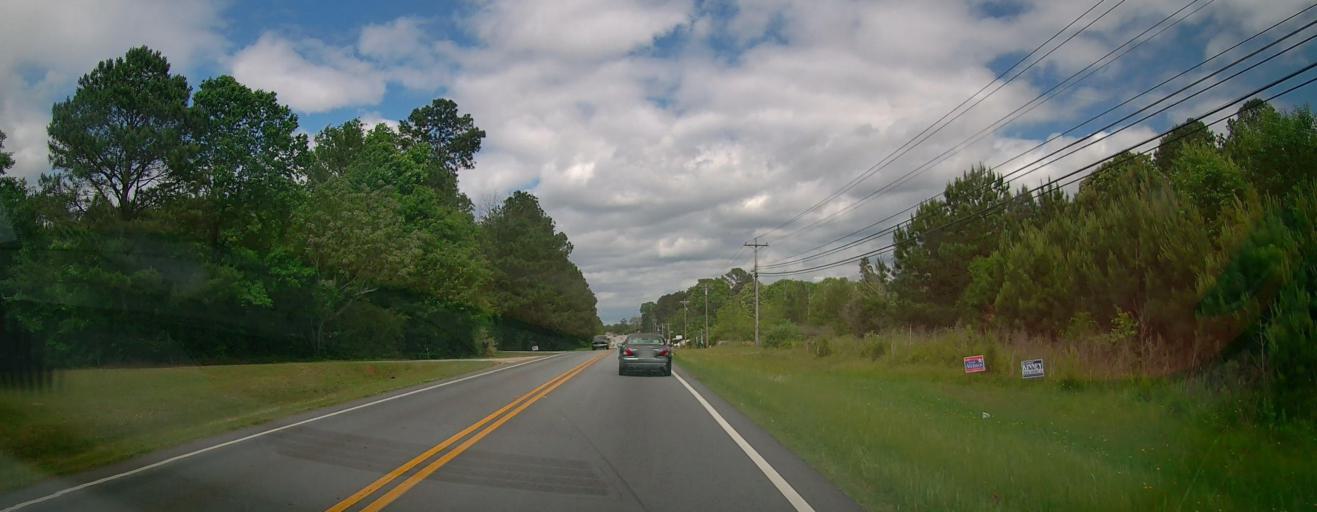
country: US
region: Georgia
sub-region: Rockdale County
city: Conyers
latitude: 33.6343
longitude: -84.0268
